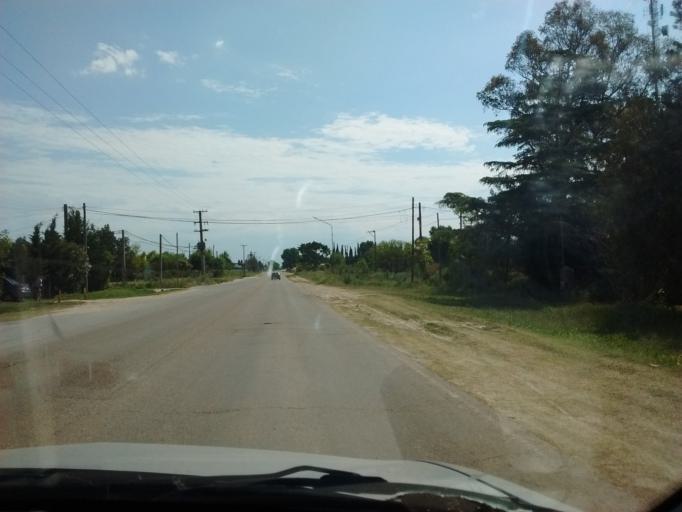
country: AR
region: Entre Rios
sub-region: Departamento de Victoria
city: Victoria
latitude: -32.6077
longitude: -60.1586
